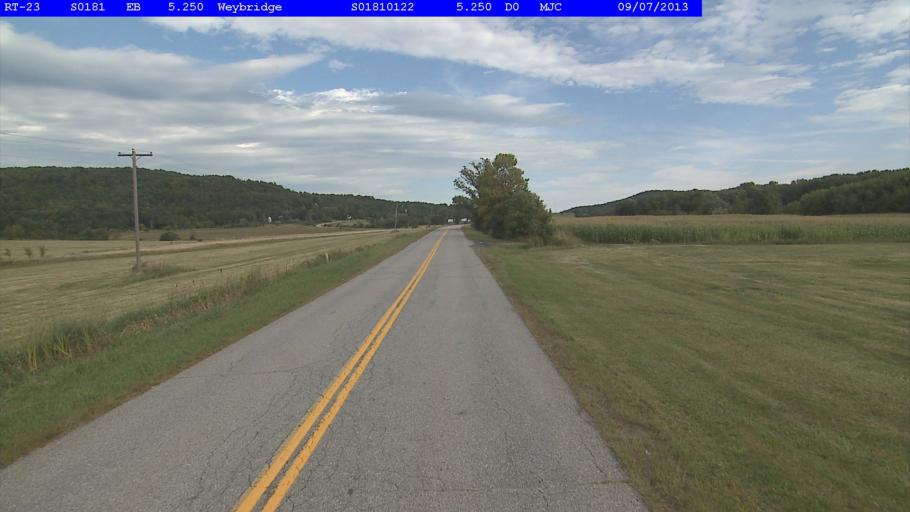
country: US
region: Vermont
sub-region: Addison County
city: Middlebury (village)
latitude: 44.0666
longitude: -73.2500
